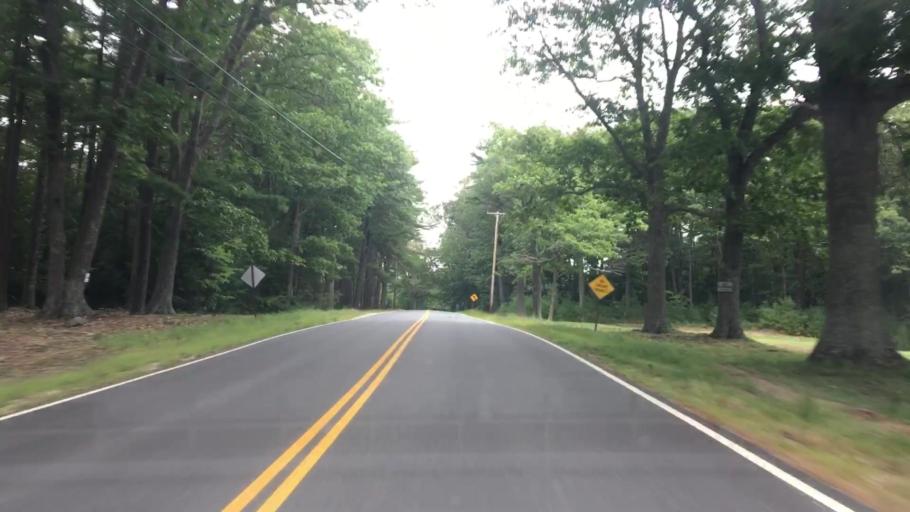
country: US
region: Maine
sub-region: Cumberland County
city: New Gloucester
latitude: 43.9029
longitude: -70.2520
